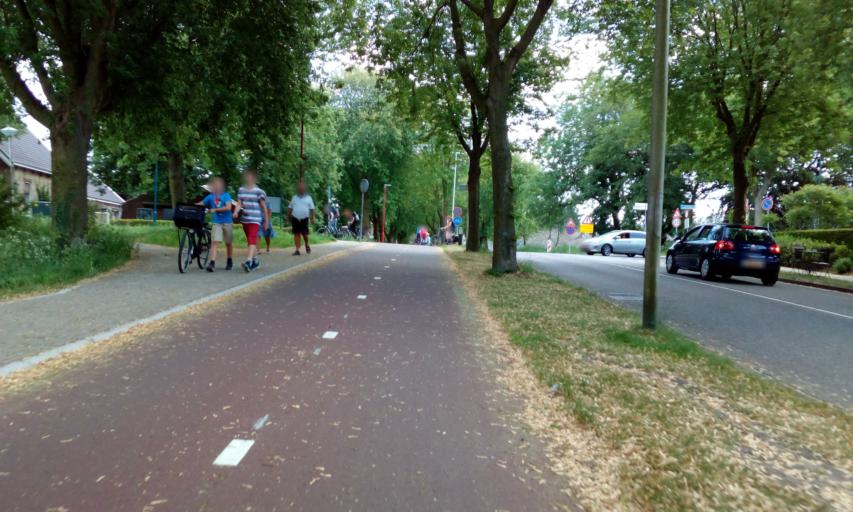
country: NL
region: South Holland
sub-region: Gemeente Zoetermeer
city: Zoetermeer
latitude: 52.0398
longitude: 4.4757
